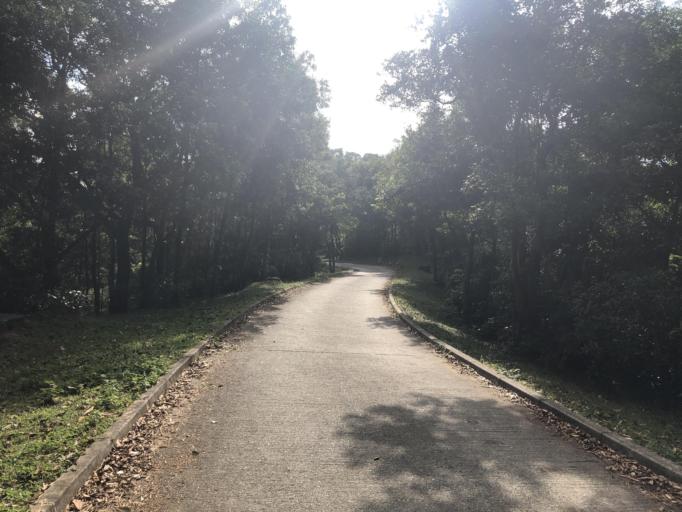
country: HK
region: Tsuen Wan
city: Tsuen Wan
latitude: 22.4047
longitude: 114.0980
